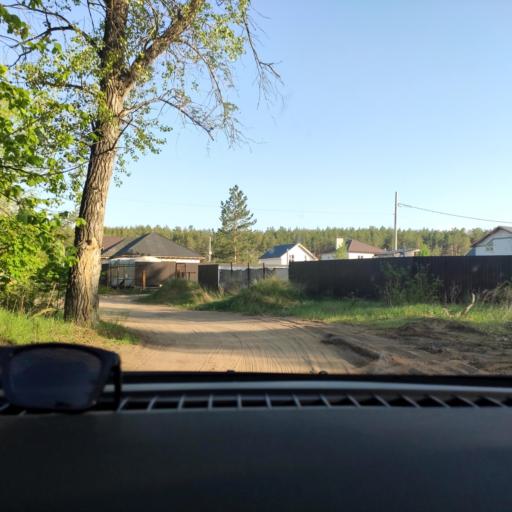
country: RU
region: Samara
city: Volzhskiy
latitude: 53.4343
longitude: 50.1607
